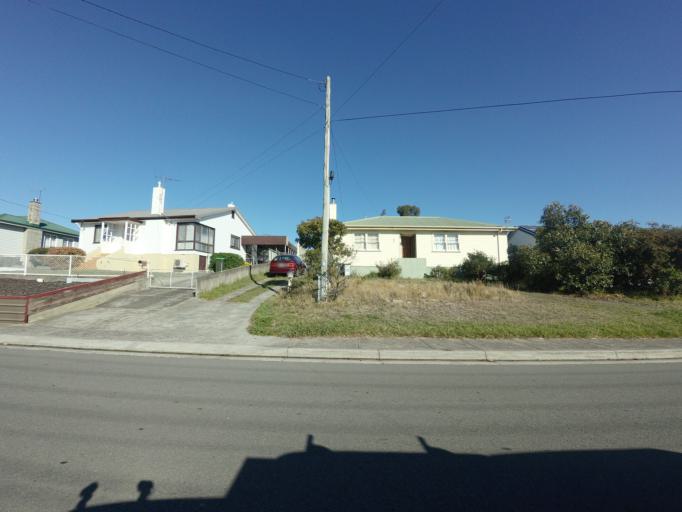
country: AU
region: Tasmania
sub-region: Clarence
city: Warrane
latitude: -42.8556
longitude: 147.3890
